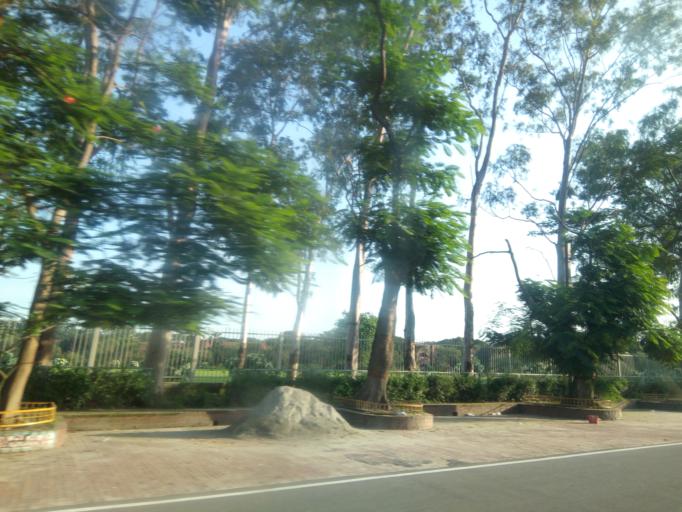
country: BD
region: Dhaka
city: Azimpur
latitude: 23.7645
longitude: 90.3767
